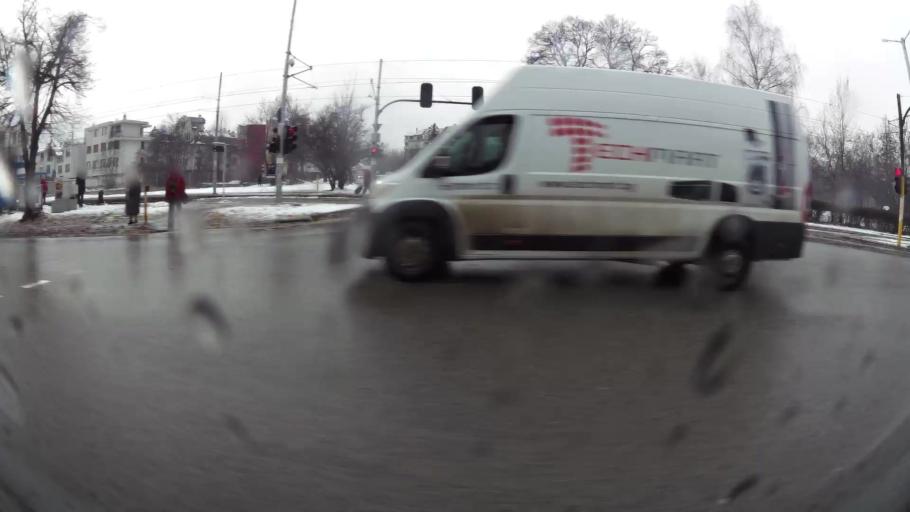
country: BG
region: Sofia-Capital
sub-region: Stolichna Obshtina
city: Sofia
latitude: 42.6771
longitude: 23.2682
